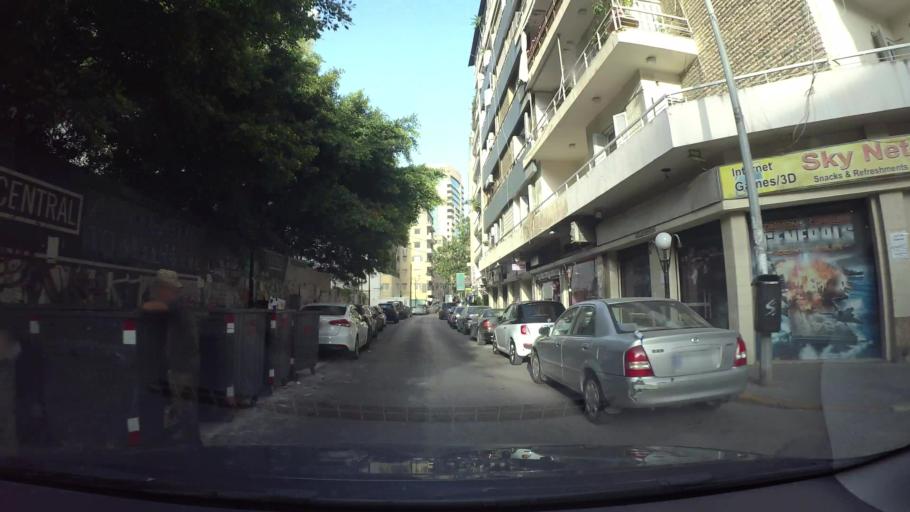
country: LB
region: Beyrouth
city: Ra's Bayrut
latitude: 33.8980
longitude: 35.4802
